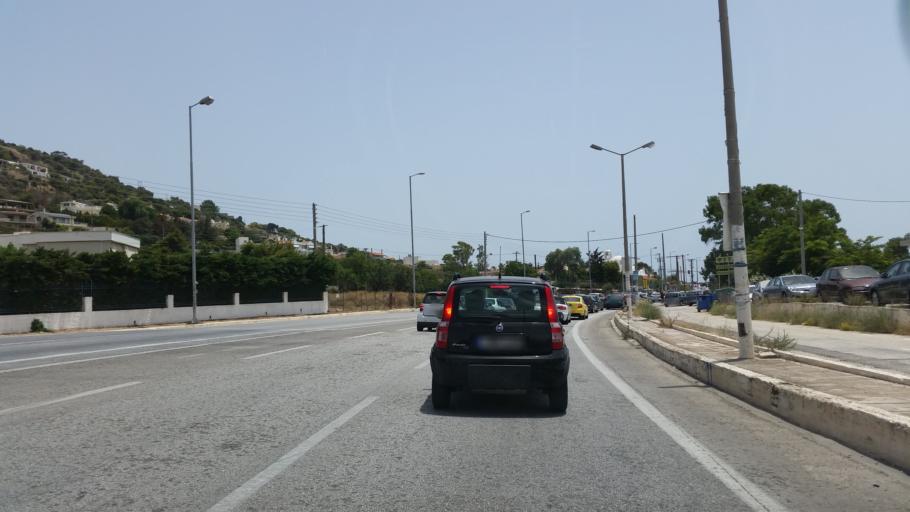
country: GR
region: Attica
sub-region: Nomarchia Anatolikis Attikis
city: Agia Marina
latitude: 37.8163
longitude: 23.8437
